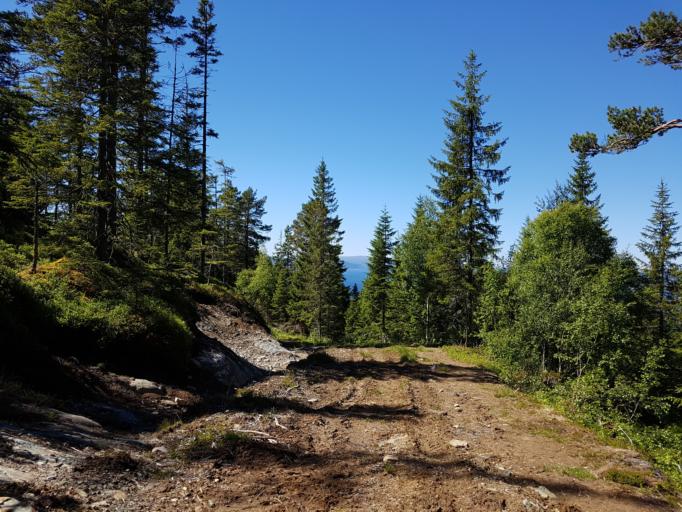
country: NO
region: Sor-Trondelag
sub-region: Melhus
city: Melhus
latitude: 63.4373
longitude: 10.2025
